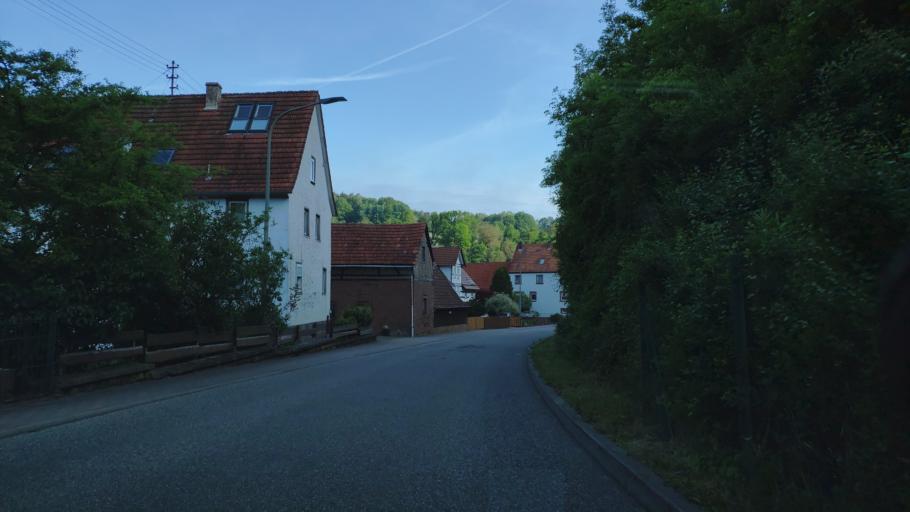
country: DE
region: Rheinland-Pfalz
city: Rumbach
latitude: 49.0941
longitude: 7.7884
